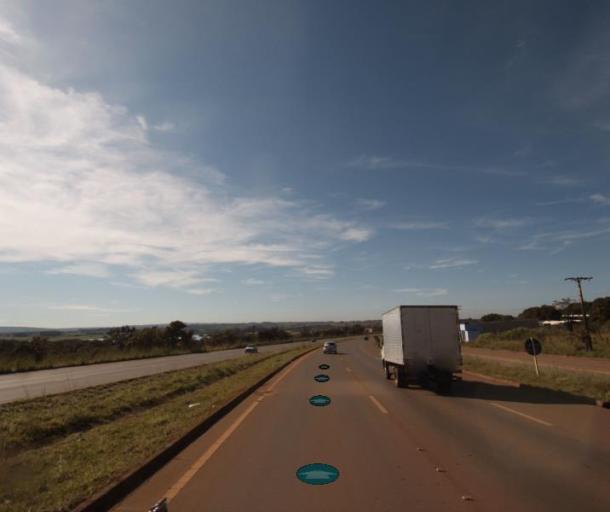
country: BR
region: Federal District
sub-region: Brasilia
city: Brasilia
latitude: -15.7634
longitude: -48.2326
